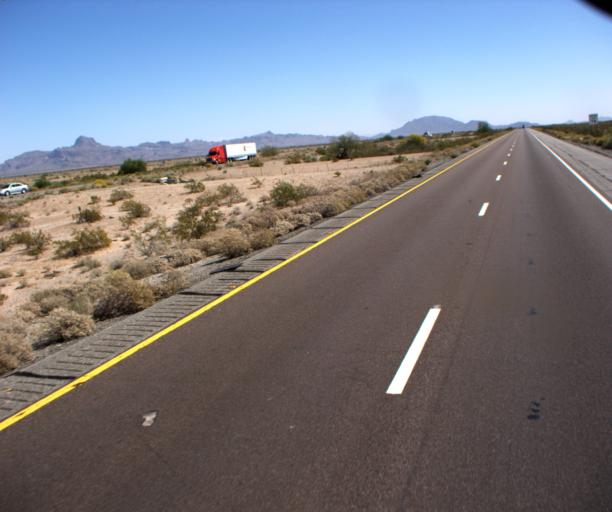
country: US
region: Arizona
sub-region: La Paz County
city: Salome
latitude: 33.5554
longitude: -113.2655
